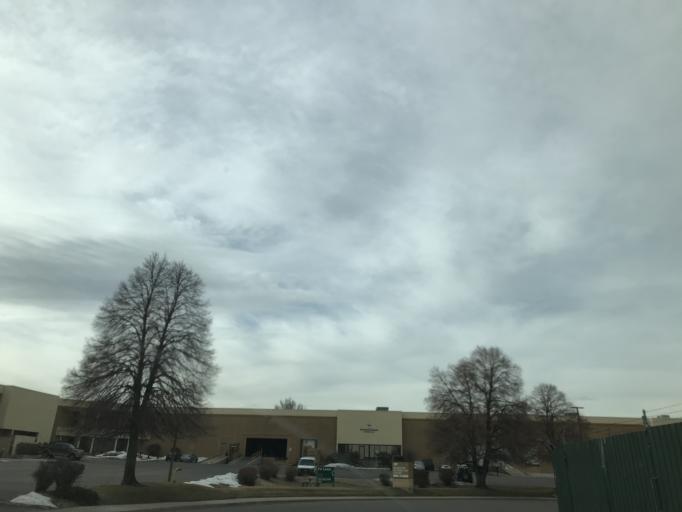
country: US
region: Colorado
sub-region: Adams County
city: Commerce City
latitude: 39.7831
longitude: -104.9170
